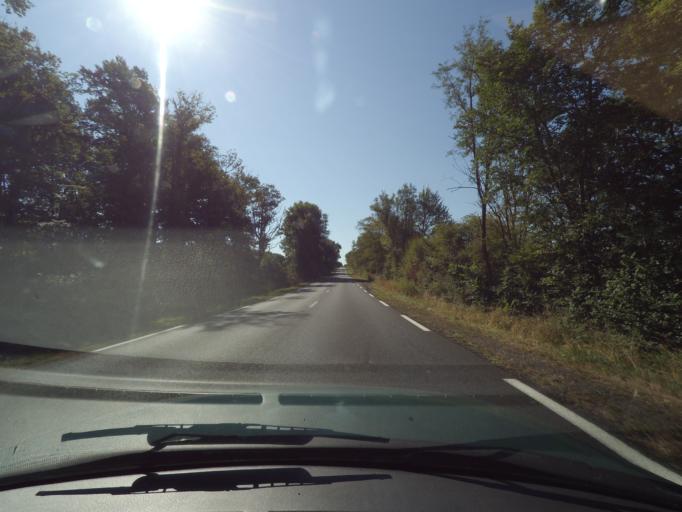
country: FR
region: Poitou-Charentes
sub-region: Departement de la Vienne
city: Lussac-les-Chateaux
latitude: 46.3526
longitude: 0.7854
